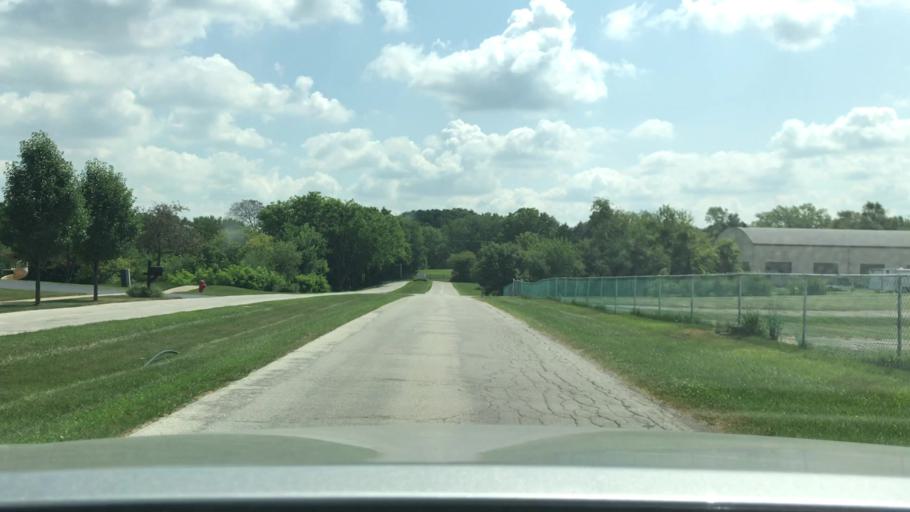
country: US
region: Illinois
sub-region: DuPage County
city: Darien
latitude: 41.7367
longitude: -87.9953
